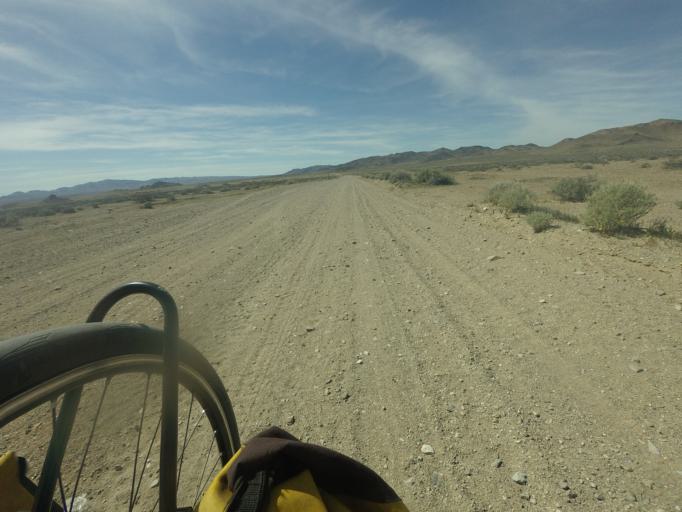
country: US
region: California
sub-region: San Bernardino County
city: Searles Valley
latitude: 35.5968
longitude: -117.4019
